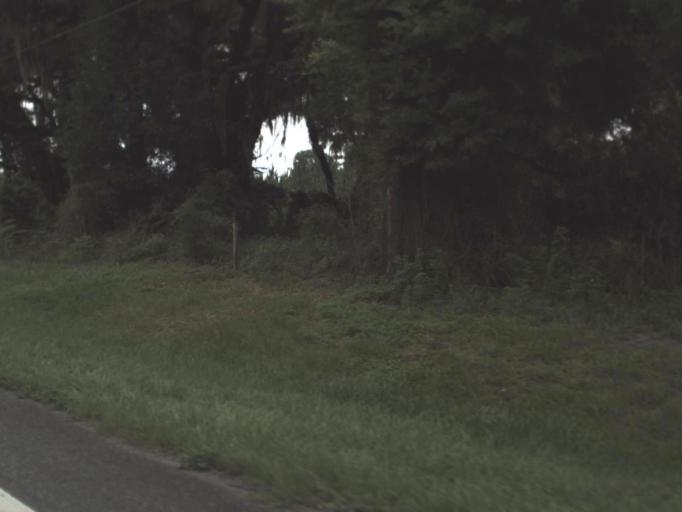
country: US
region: Florida
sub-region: Alachua County
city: Archer
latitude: 29.4901
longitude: -82.4930
